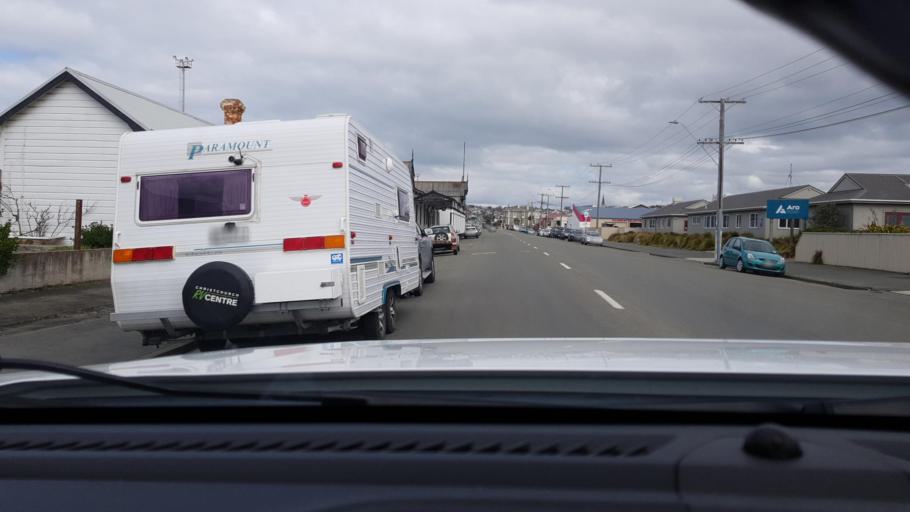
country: NZ
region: Otago
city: Oamaru
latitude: -45.0950
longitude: 170.9759
